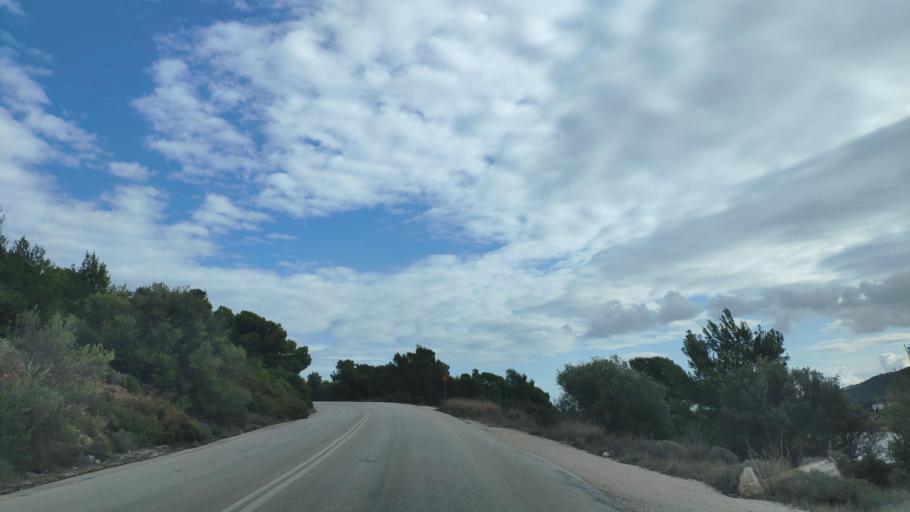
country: GR
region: Attica
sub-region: Nomarchia Anatolikis Attikis
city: Limin Mesoyaias
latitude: 37.9289
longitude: 24.0013
